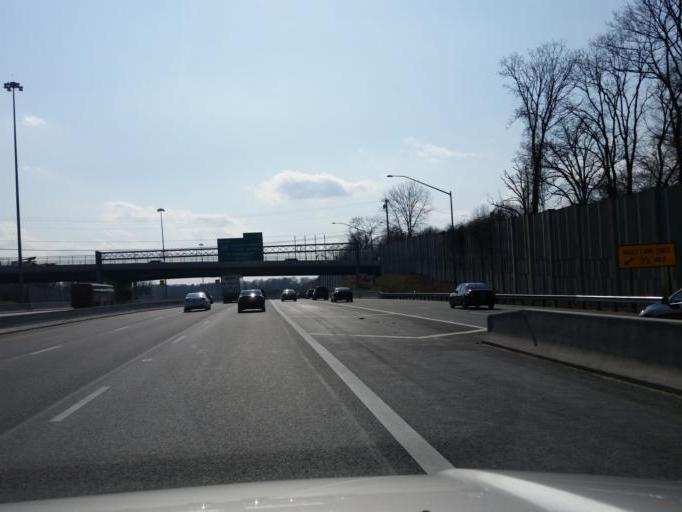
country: US
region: Maryland
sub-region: Baltimore County
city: Overlea
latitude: 39.3471
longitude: -76.5056
